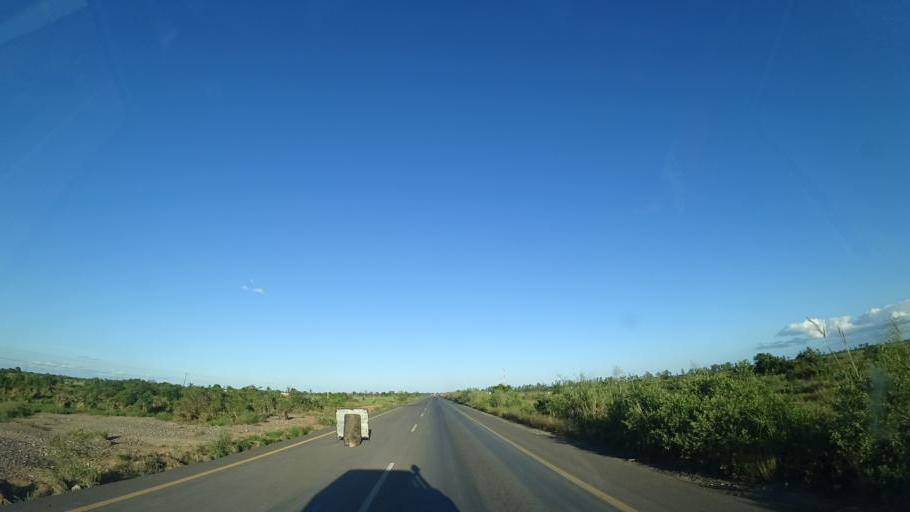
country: MZ
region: Sofala
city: Dondo
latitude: -19.3264
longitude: 34.3053
